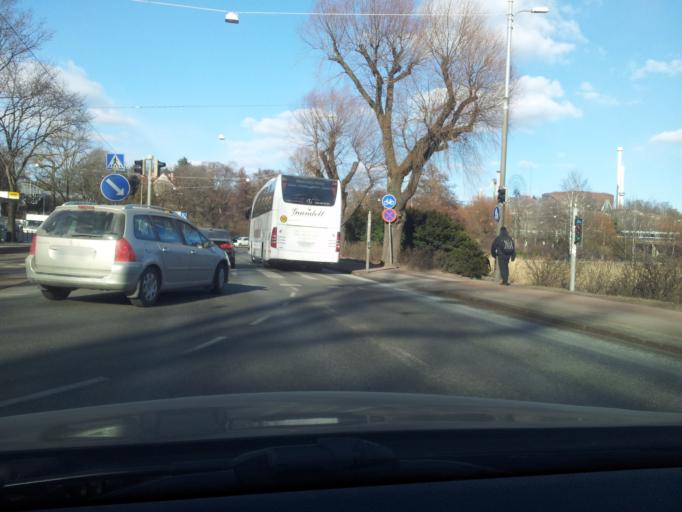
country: FI
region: Uusimaa
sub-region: Helsinki
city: Helsinki
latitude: 60.1840
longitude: 24.9319
